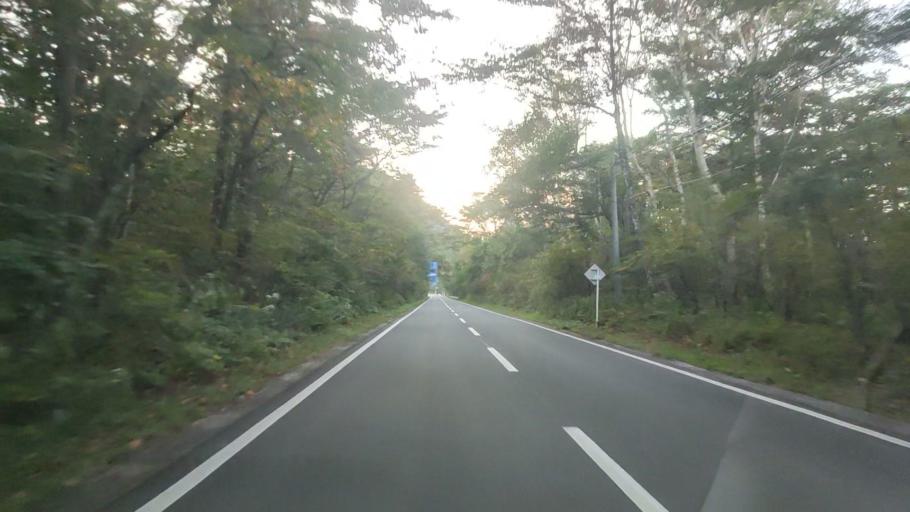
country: JP
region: Nagano
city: Komoro
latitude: 36.4011
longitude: 138.5722
